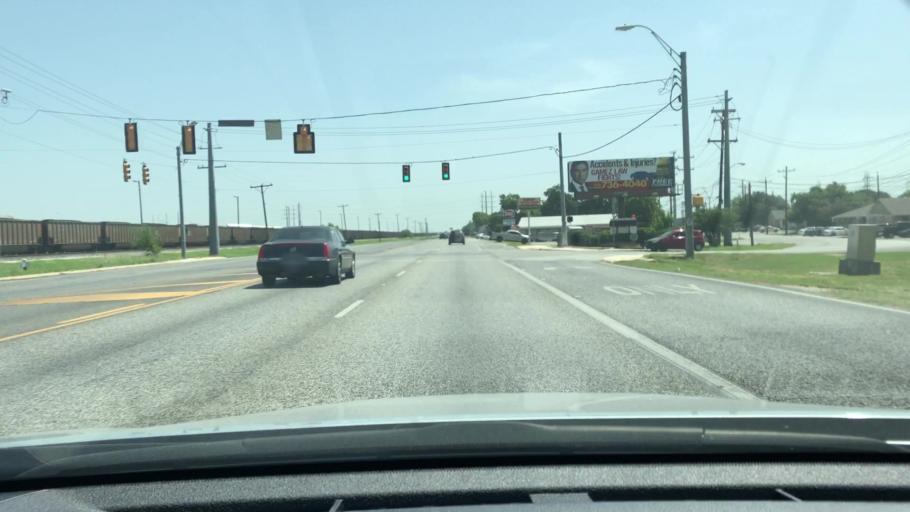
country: US
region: Texas
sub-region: Bexar County
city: Kirby
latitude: 29.4638
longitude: -98.3978
